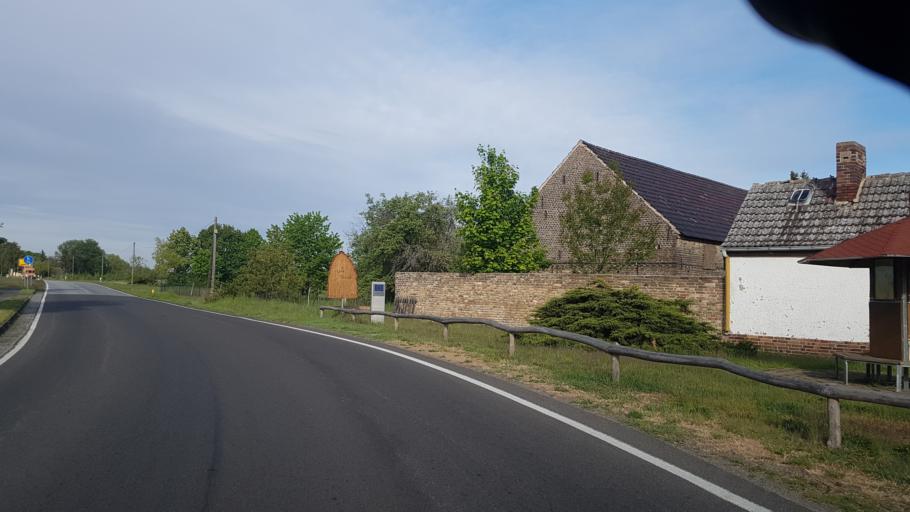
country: DE
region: Brandenburg
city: Baruth
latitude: 52.0527
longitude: 13.4291
